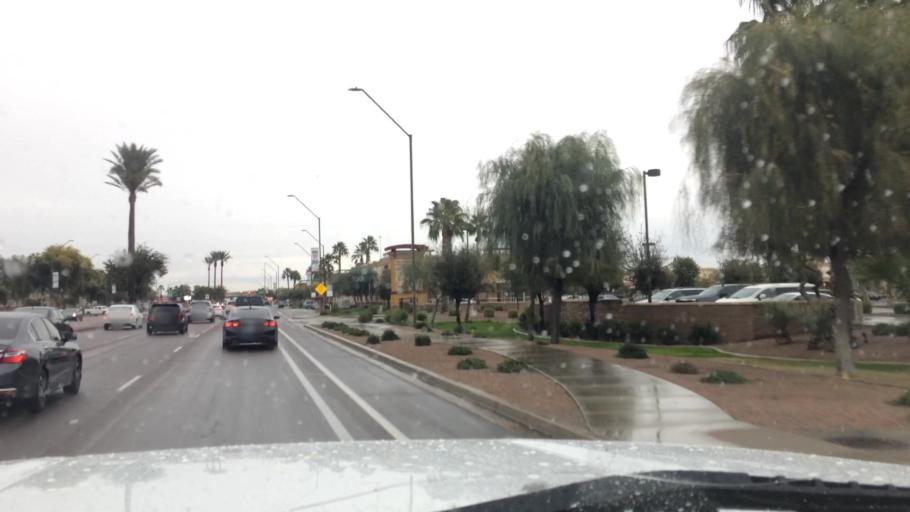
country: US
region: Arizona
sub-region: Maricopa County
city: Tolleson
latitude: 33.4646
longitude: -112.2767
